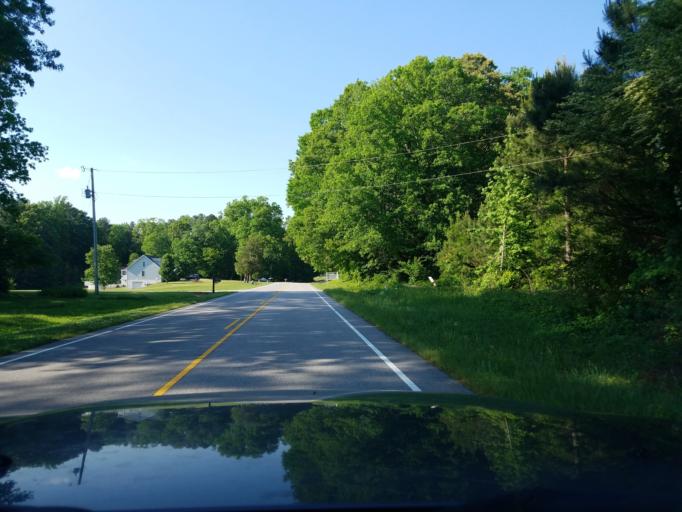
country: US
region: North Carolina
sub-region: Vance County
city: Henderson
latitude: 36.3838
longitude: -78.3689
